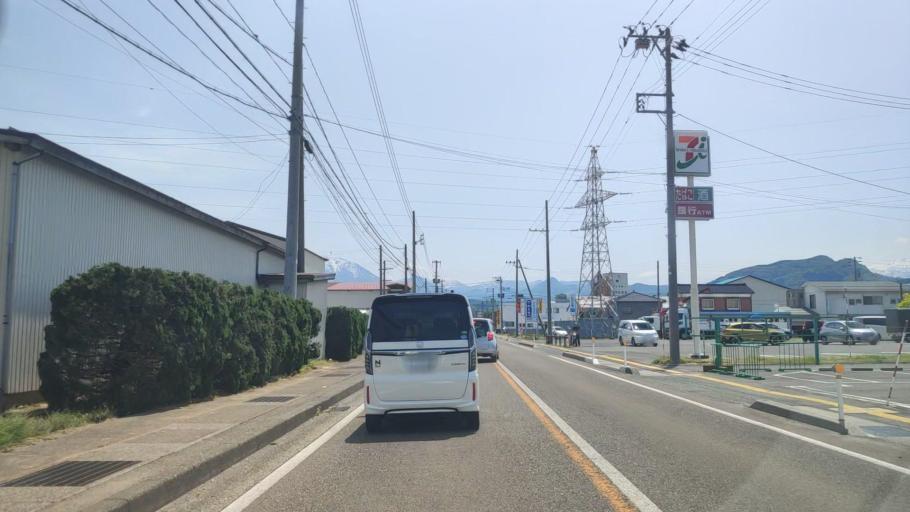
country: JP
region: Niigata
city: Itoigawa
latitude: 37.0170
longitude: 137.8633
